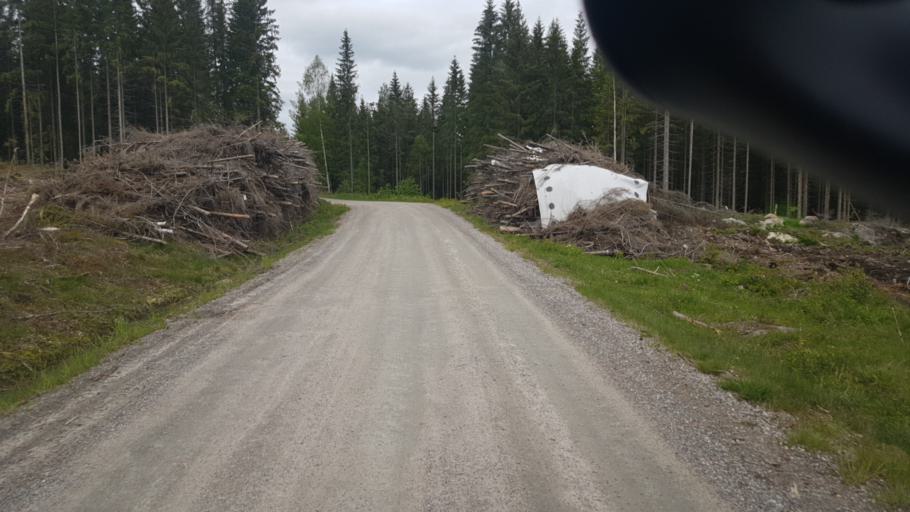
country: SE
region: Vaermland
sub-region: Eda Kommun
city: Amotfors
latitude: 59.8411
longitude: 12.5338
